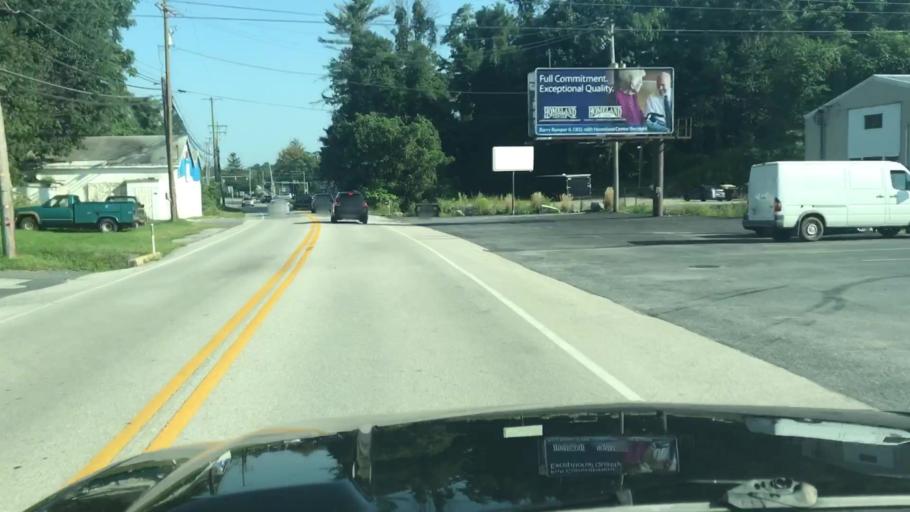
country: US
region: Pennsylvania
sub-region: York County
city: Valley Green
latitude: 40.1739
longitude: -76.8298
